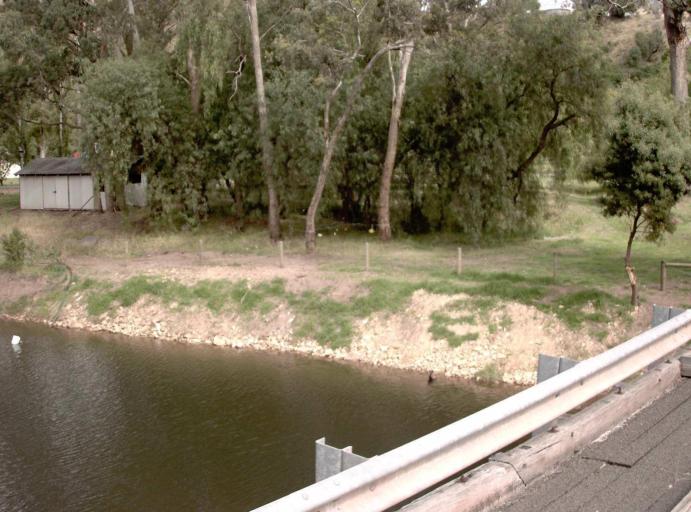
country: AU
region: Victoria
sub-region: Wellington
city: Heyfield
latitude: -37.6291
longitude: 146.6230
